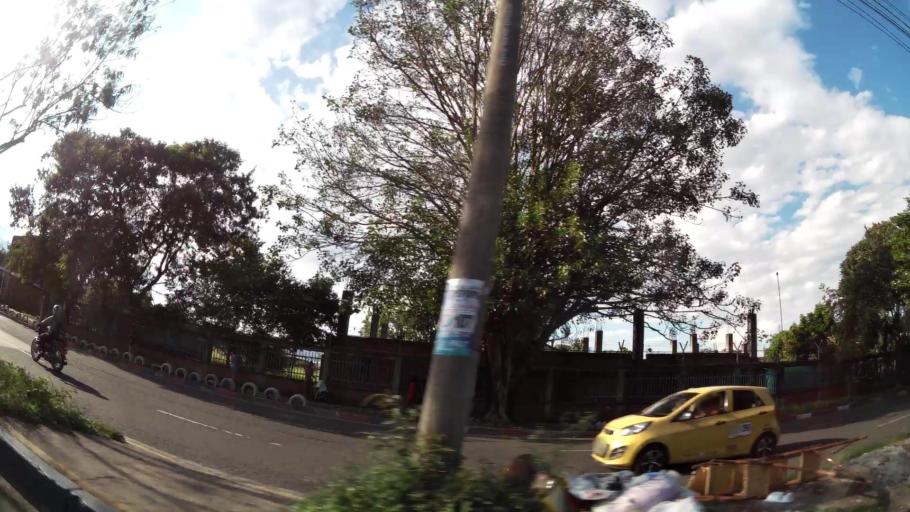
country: CO
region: Valle del Cauca
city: Cali
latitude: 3.4084
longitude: -76.4966
